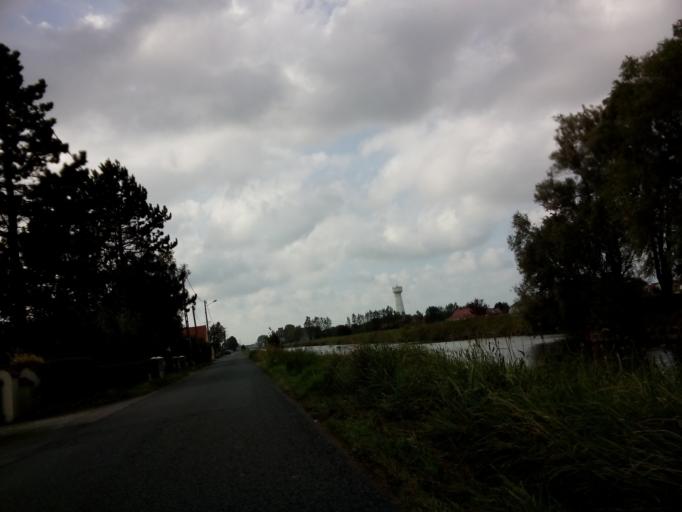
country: FR
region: Nord-Pas-de-Calais
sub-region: Departement du Pas-de-Calais
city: Les Attaques
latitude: 50.9030
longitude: 1.9428
